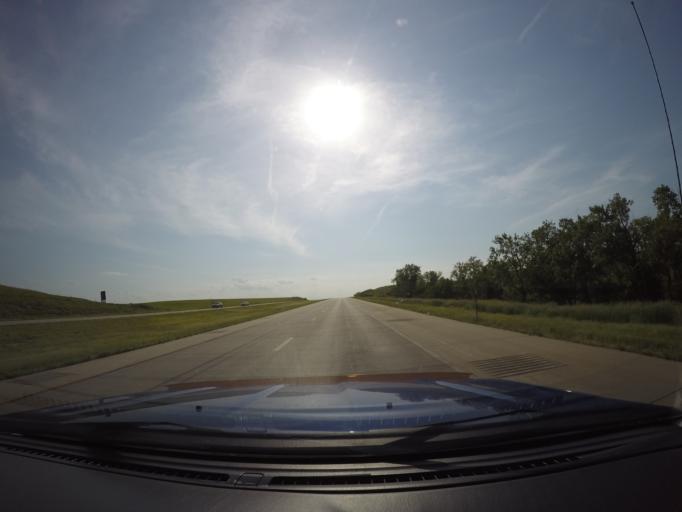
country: US
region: Kansas
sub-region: Wabaunsee County
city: Alma
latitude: 39.0659
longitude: -96.3111
